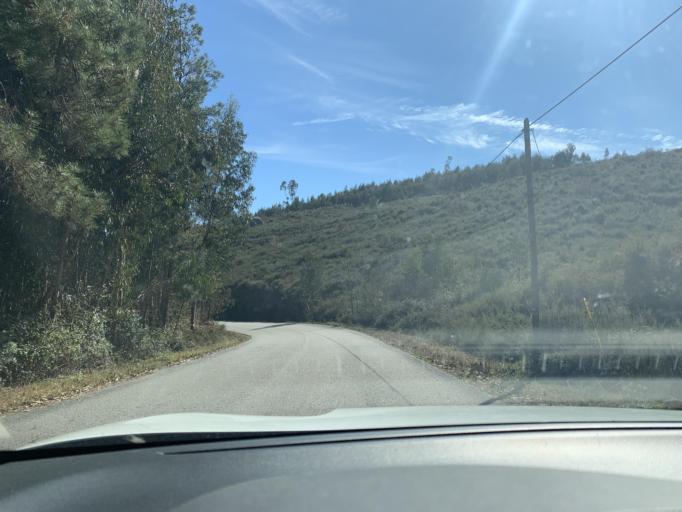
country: PT
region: Viseu
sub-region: Concelho de Tondela
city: Tondela
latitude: 40.6032
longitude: -8.0314
